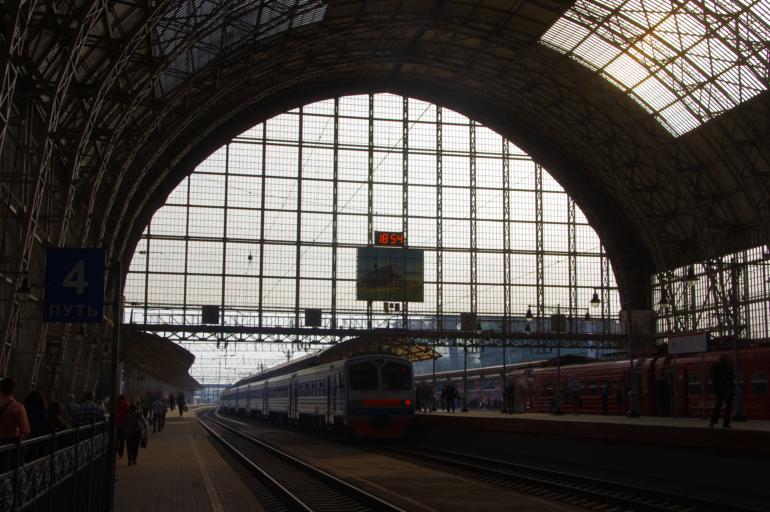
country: RU
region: Moskovskaya
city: Dorogomilovo
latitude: 55.7425
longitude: 37.5653
